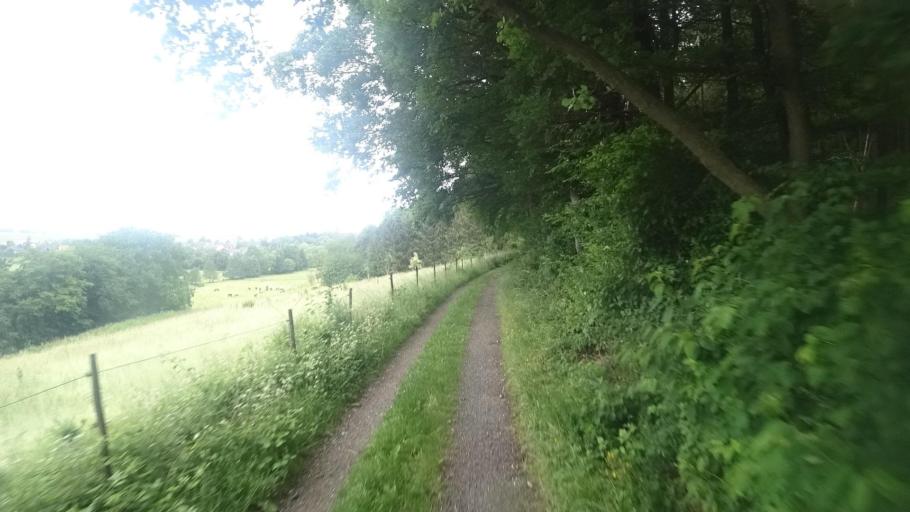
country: DE
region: Rheinland-Pfalz
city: Dernau
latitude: 50.5526
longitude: 7.0503
